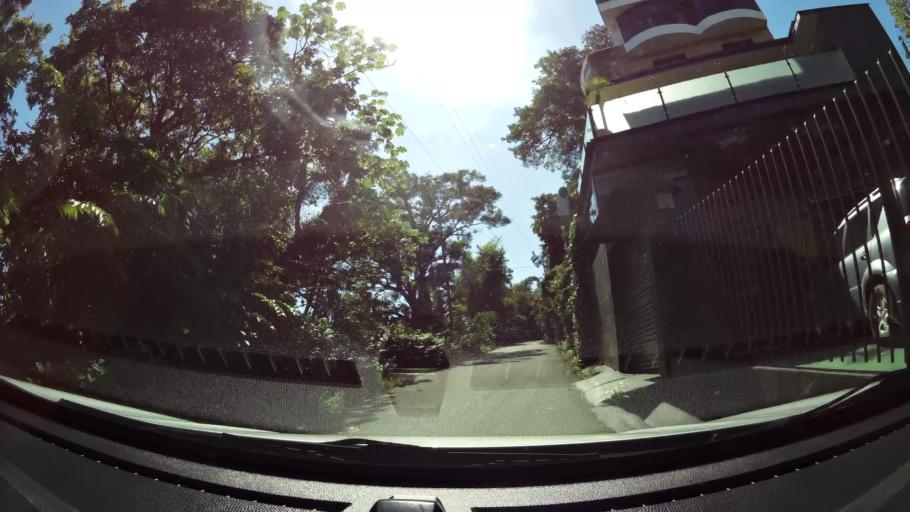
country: CR
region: Puntarenas
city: Quepos
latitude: 9.4016
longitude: -84.1624
